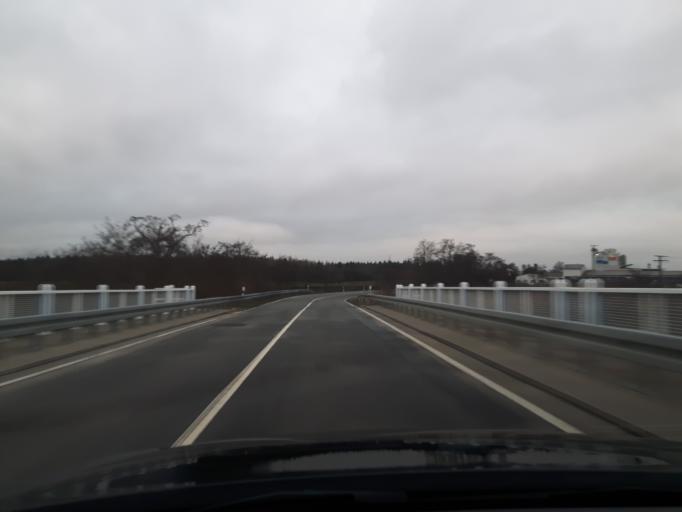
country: DE
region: Mecklenburg-Vorpommern
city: Tribsees
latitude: 54.0694
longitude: 12.7163
